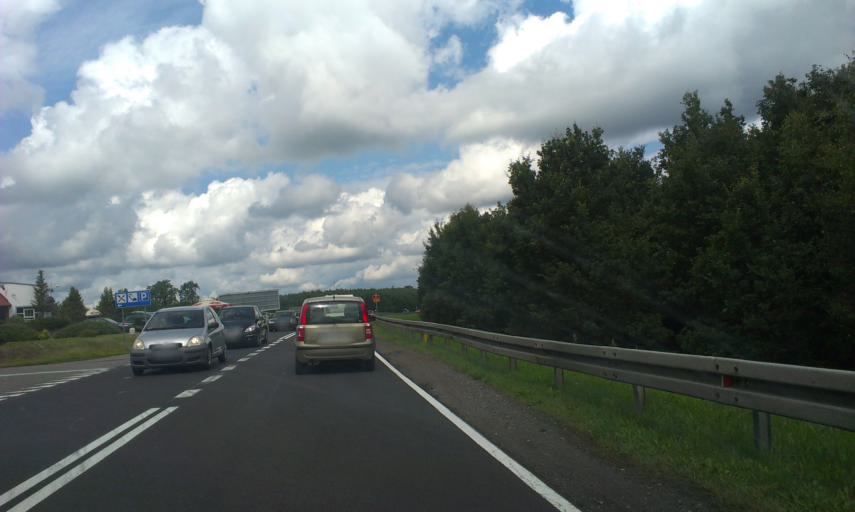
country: PL
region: West Pomeranian Voivodeship
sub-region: Powiat koszalinski
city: Bobolice
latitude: 53.9739
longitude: 16.5529
